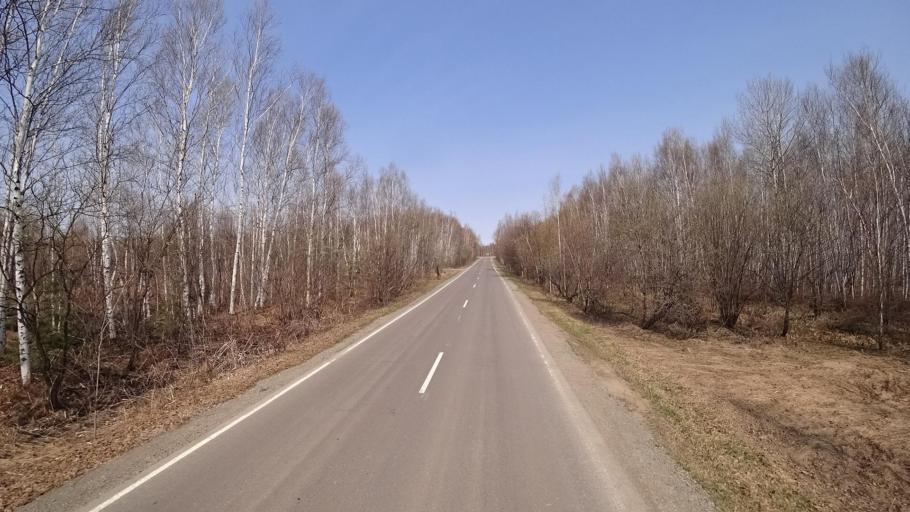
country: RU
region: Khabarovsk Krai
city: Selikhino
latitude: 50.3934
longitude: 137.3742
